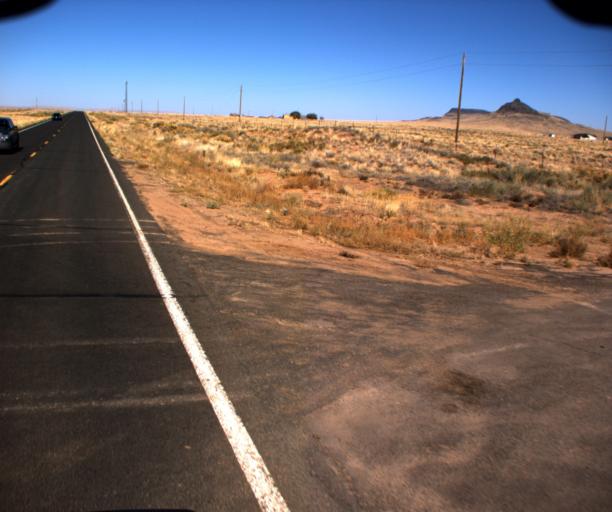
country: US
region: Arizona
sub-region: Navajo County
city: Dilkon
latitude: 35.5070
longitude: -110.4369
